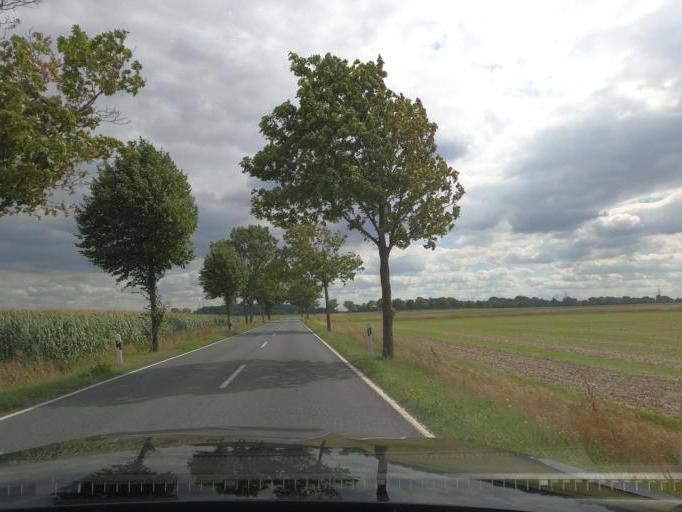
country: DE
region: Lower Saxony
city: Lehrte
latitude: 52.3539
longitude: 10.0252
